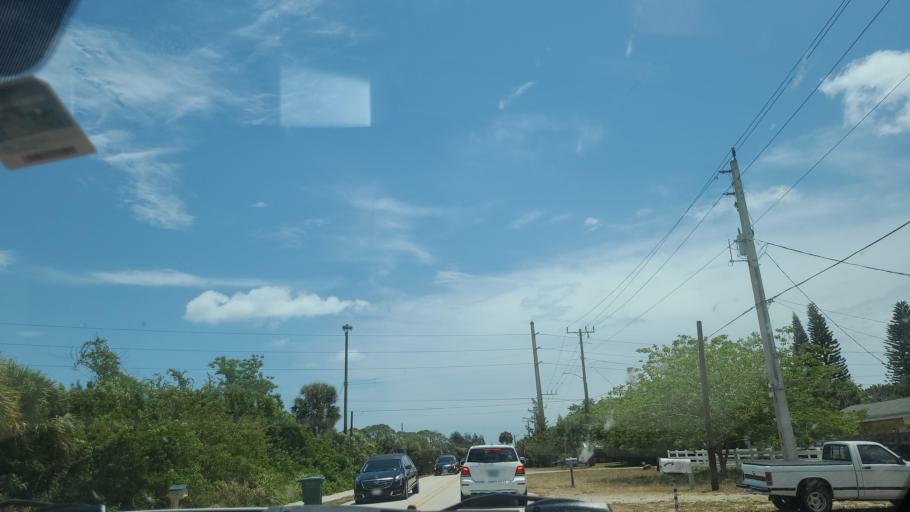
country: US
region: Florida
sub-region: Brevard County
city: Grant-Valkaria
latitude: 27.9638
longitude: -80.5479
